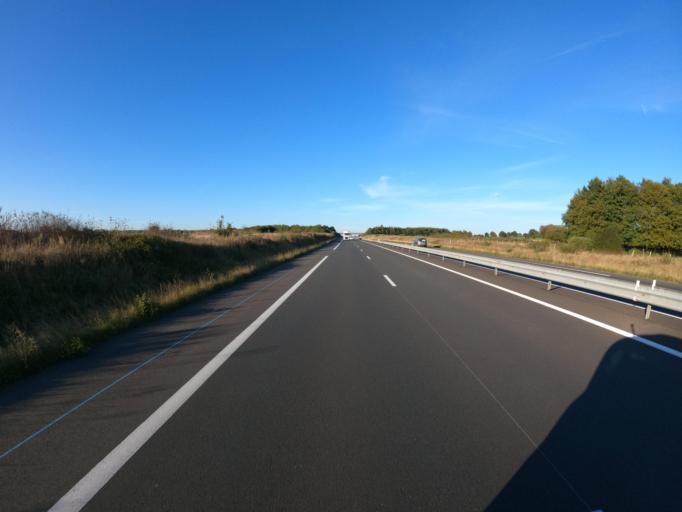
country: FR
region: Pays de la Loire
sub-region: Departement de la Vendee
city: Saint-Fulgent
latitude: 46.8523
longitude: -1.1448
